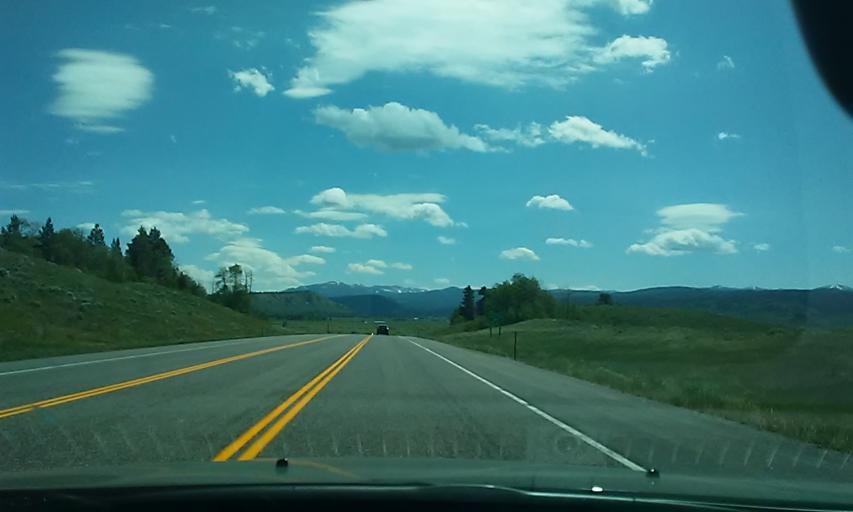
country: US
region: Wyoming
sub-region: Teton County
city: Jackson
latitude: 43.8387
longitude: -110.4457
